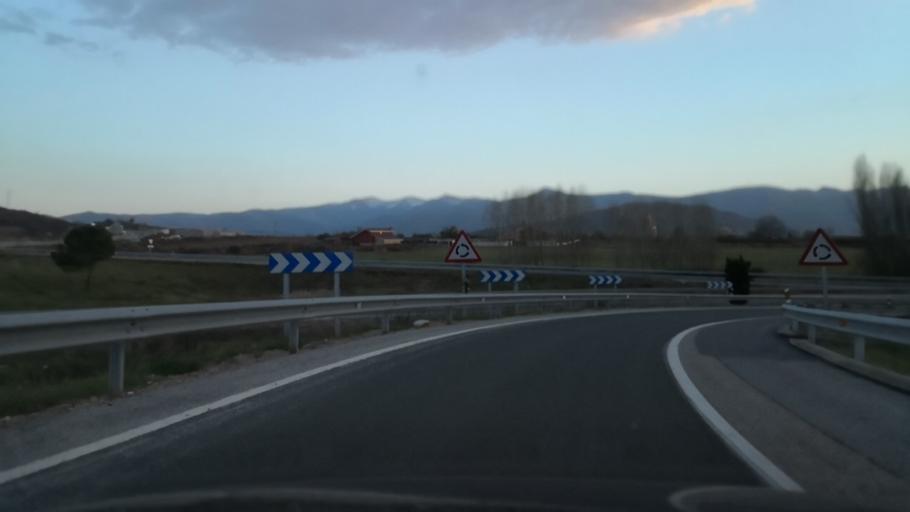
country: ES
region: Castille and Leon
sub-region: Provincia de Leon
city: Ponferrada
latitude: 42.5800
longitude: -6.6059
